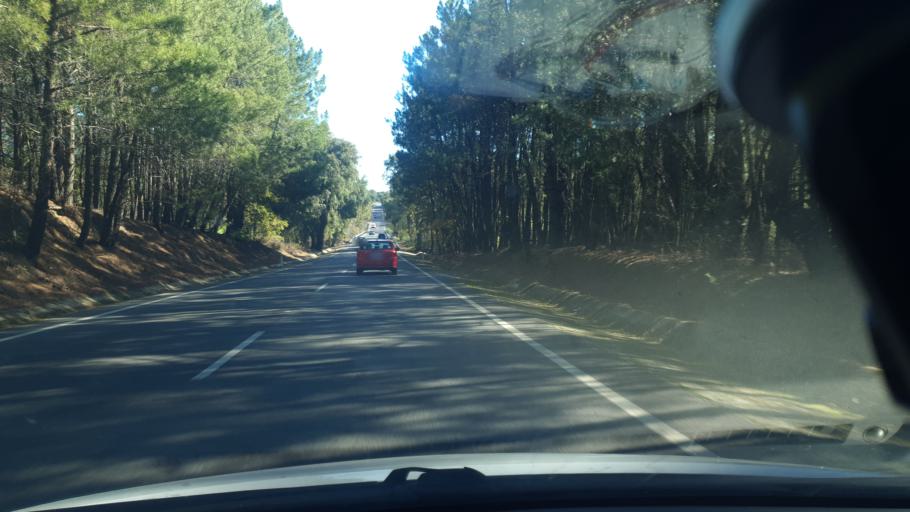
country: ES
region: Castille and Leon
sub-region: Provincia de Avila
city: Piedralaves
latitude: 40.3145
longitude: -4.6715
